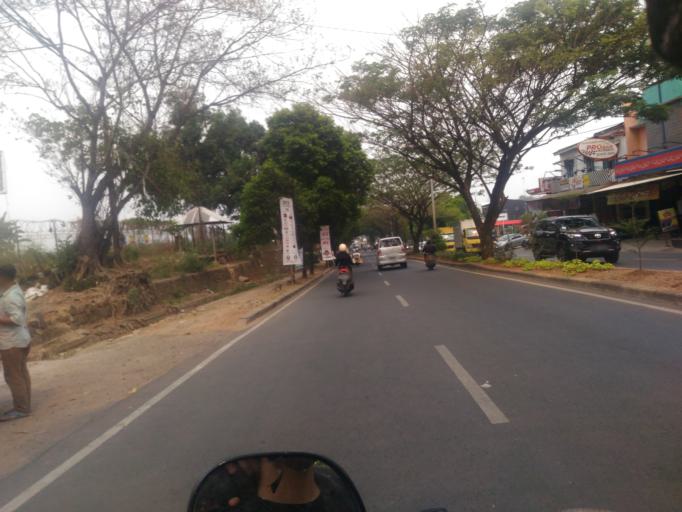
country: ID
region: West Java
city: Depok
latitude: -6.3805
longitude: 106.8555
